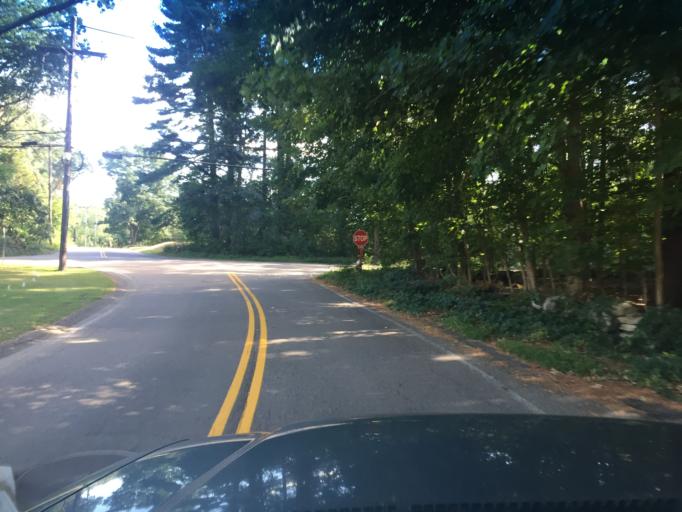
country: US
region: Massachusetts
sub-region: Norfolk County
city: Millis
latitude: 42.1847
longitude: -71.3722
